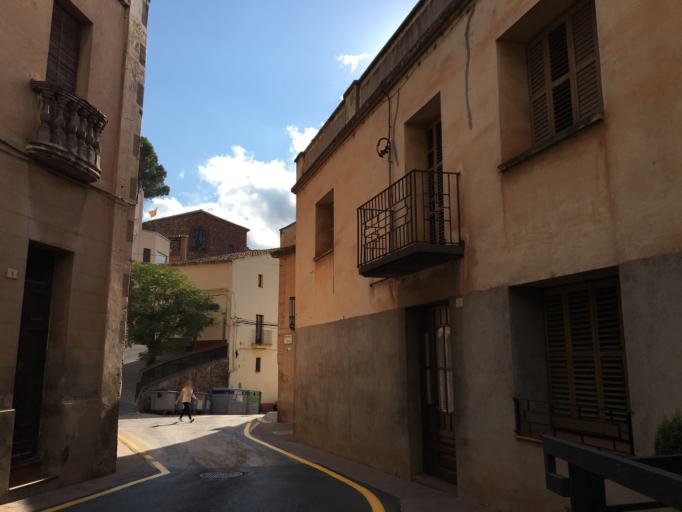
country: ES
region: Catalonia
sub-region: Provincia de Barcelona
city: Corbera de Llobregat
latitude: 41.4177
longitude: 1.9215
